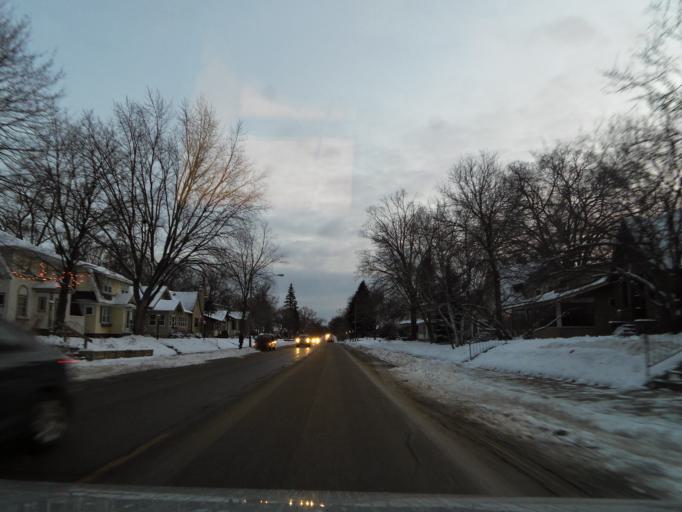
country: US
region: Minnesota
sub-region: Hennepin County
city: Edina
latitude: 44.9082
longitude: -93.3190
